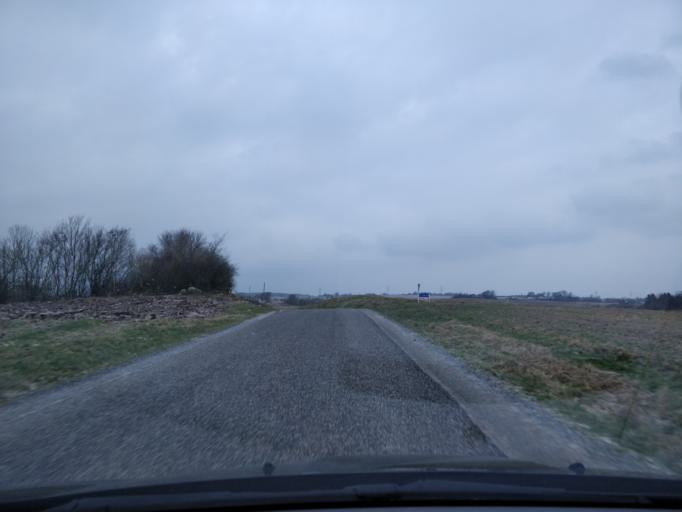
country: DK
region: South Denmark
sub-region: Vejle Kommune
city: Vejle
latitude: 55.7713
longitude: 9.5483
